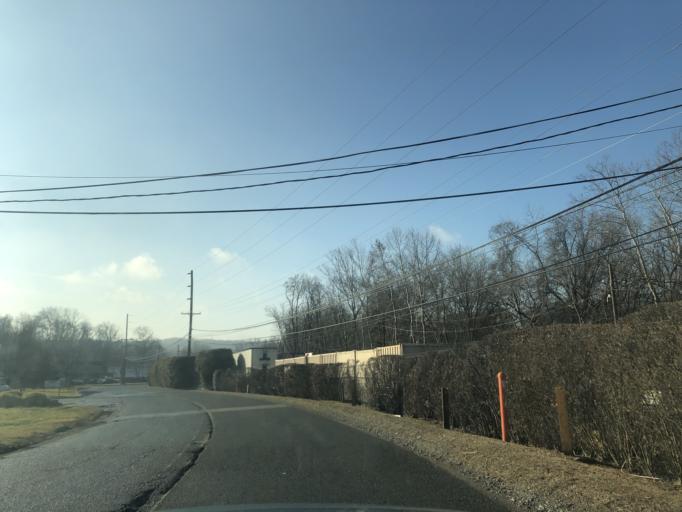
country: US
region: Pennsylvania
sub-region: Montgomery County
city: Conshohocken
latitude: 40.0815
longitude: -75.3111
